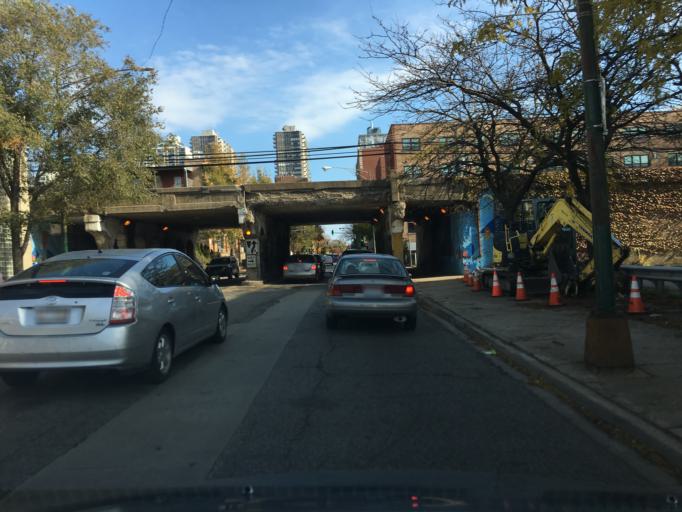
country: US
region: Illinois
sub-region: Cook County
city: Evanston
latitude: 41.9854
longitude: -87.6595
